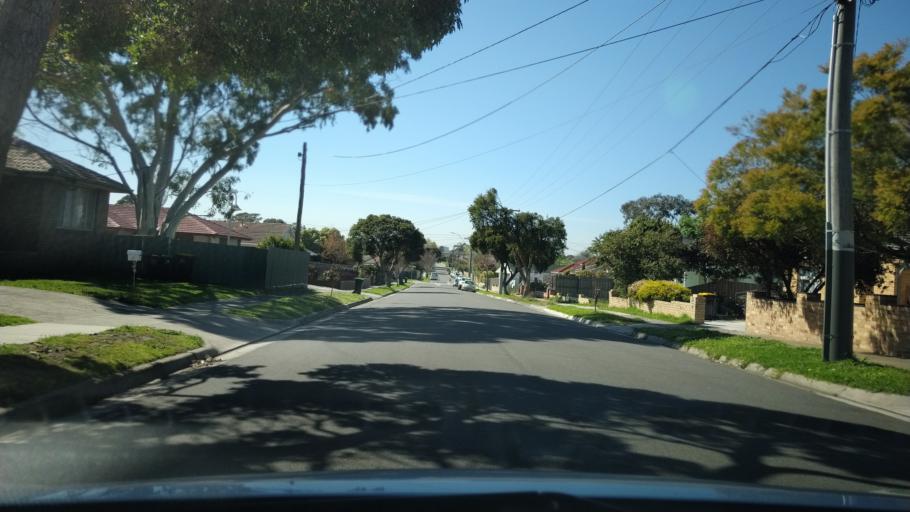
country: AU
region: Victoria
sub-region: Greater Dandenong
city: Noble Park
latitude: -37.9577
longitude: 145.1772
